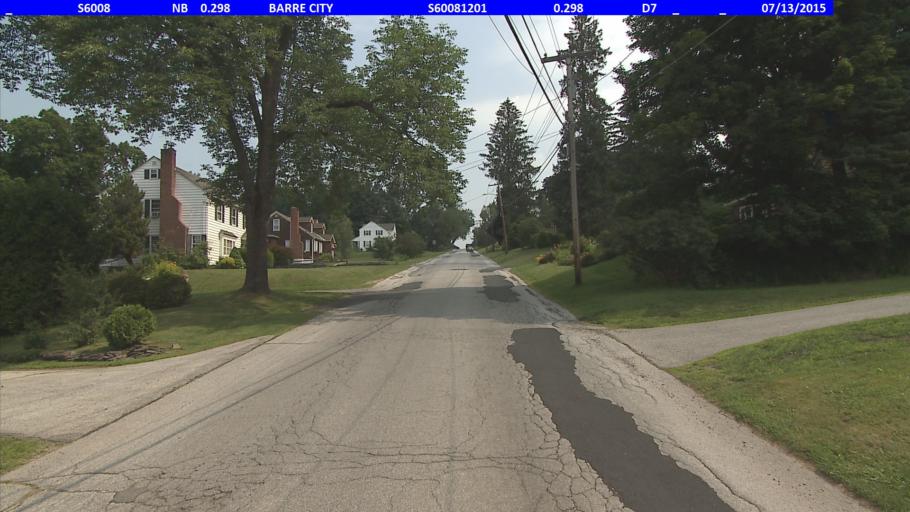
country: US
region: Vermont
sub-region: Washington County
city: Barre
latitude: 44.1971
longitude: -72.4893
